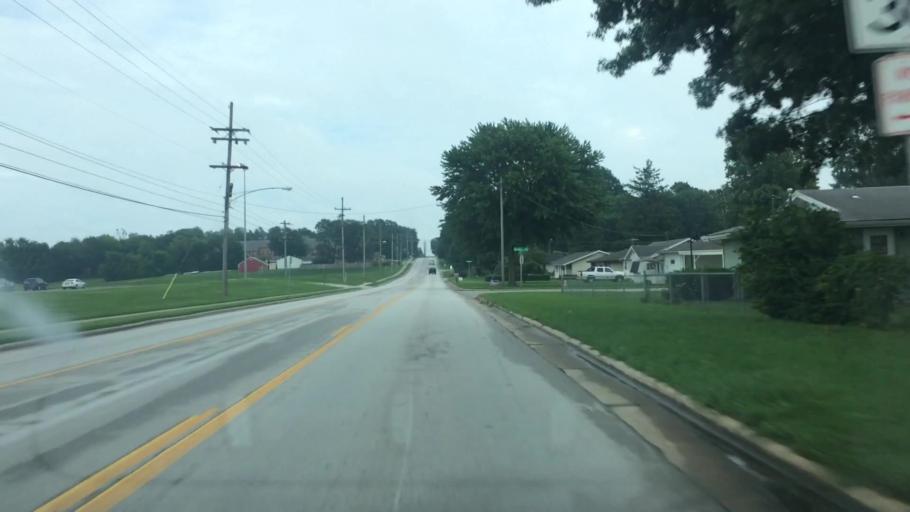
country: US
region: Missouri
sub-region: Greene County
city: Springfield
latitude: 37.2176
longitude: -93.2449
